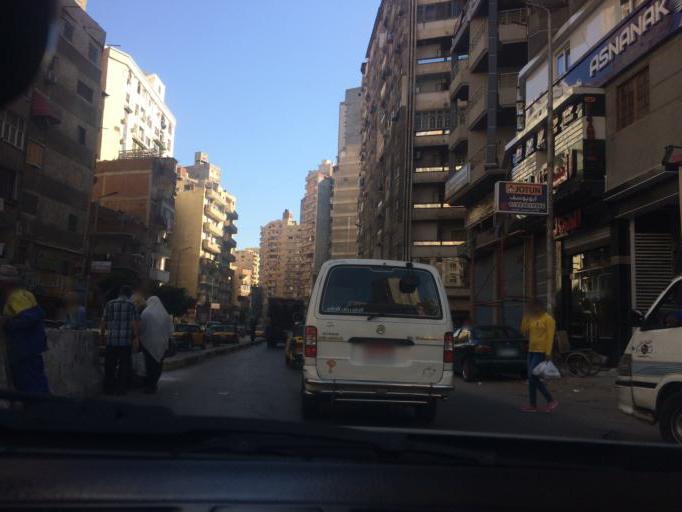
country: EG
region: Alexandria
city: Alexandria
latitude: 31.2556
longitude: 29.9846
